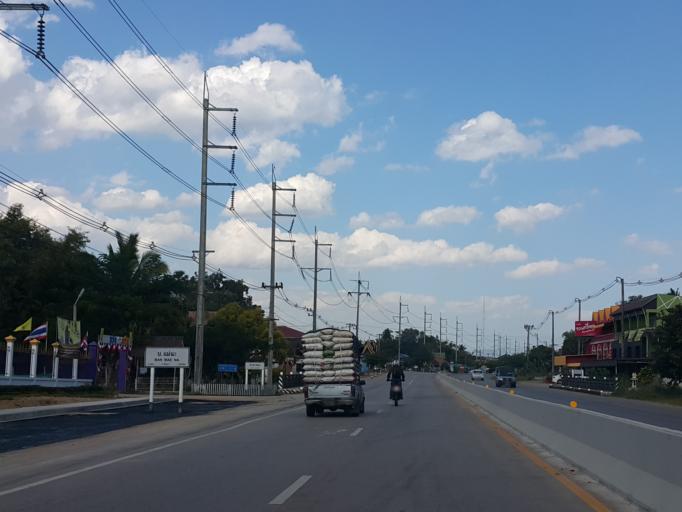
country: TH
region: Chiang Mai
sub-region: Amphoe Chiang Dao
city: Chiang Dao
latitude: 19.3252
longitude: 98.9540
